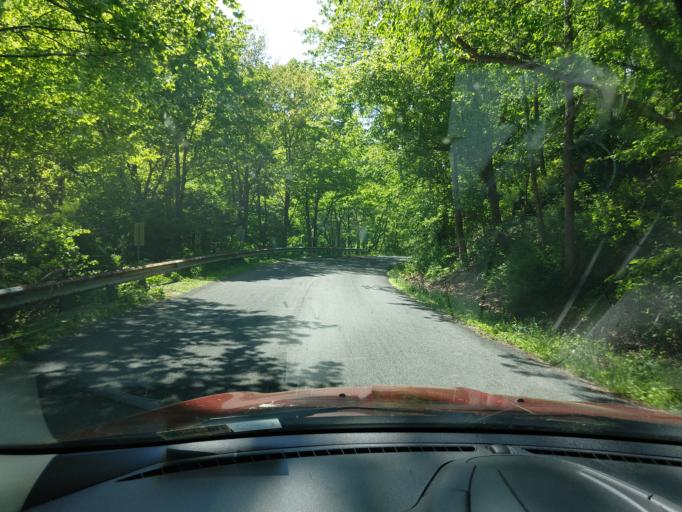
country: US
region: Virginia
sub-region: City of Covington
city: Fairlawn
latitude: 37.7122
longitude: -79.9100
